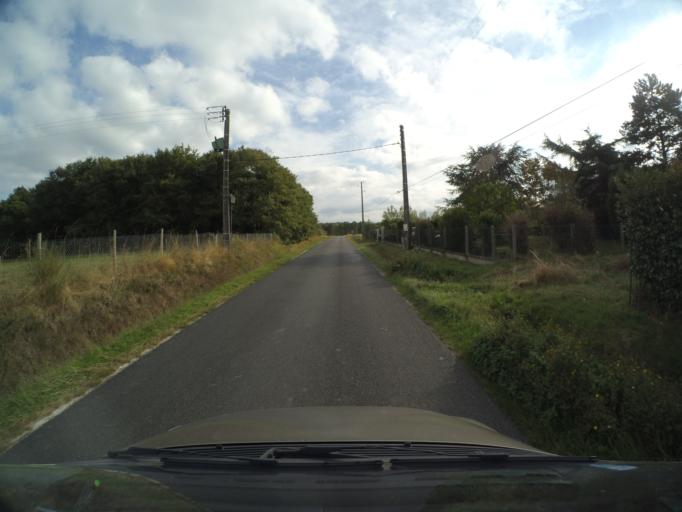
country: FR
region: Centre
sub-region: Departement d'Indre-et-Loire
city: Nazelles-Negron
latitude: 47.4699
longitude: 0.9543
